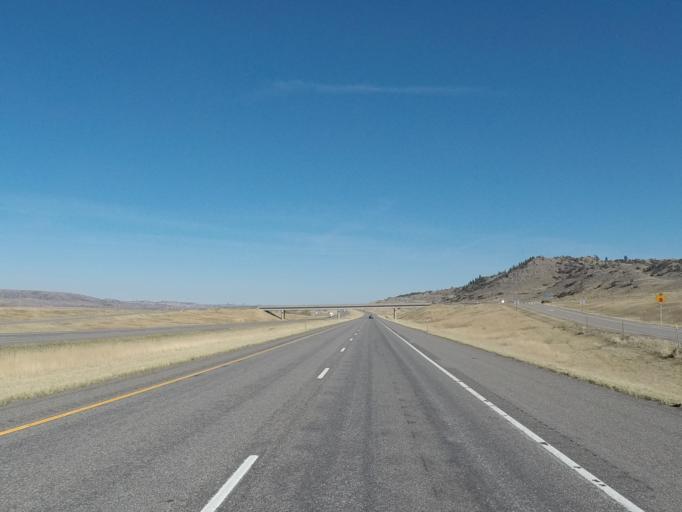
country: US
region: Montana
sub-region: Sweet Grass County
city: Big Timber
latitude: 45.7764
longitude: -110.0694
